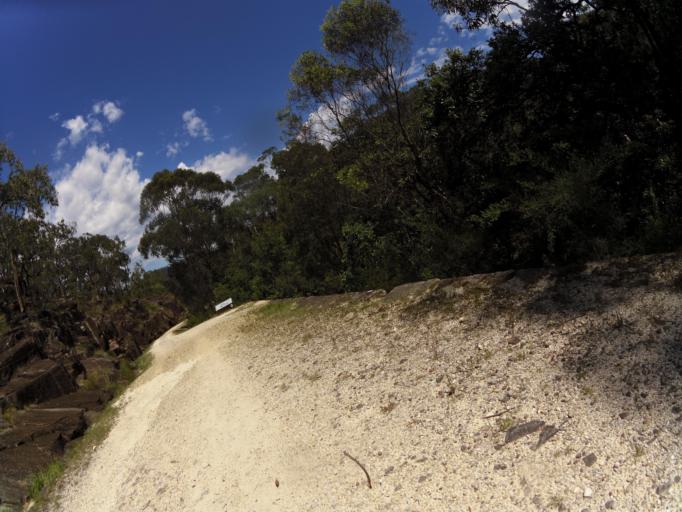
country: AU
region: New South Wales
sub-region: Hornsby Shire
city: Glenorie
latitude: -33.3684
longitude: 150.9870
